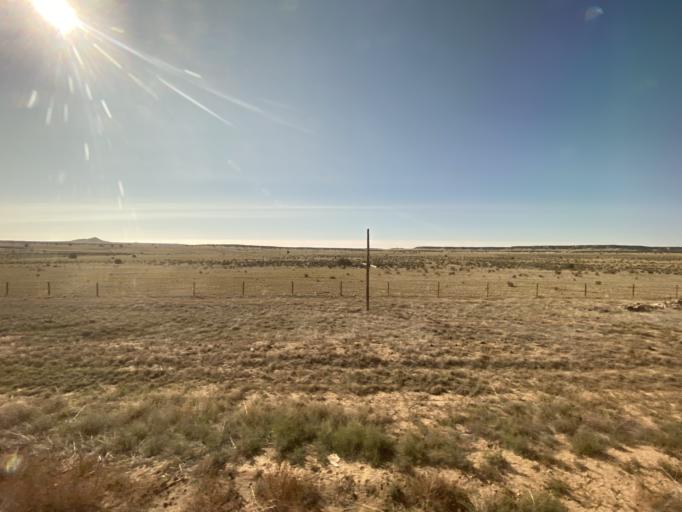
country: US
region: Colorado
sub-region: Otero County
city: Fowler
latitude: 37.5706
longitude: -104.0606
